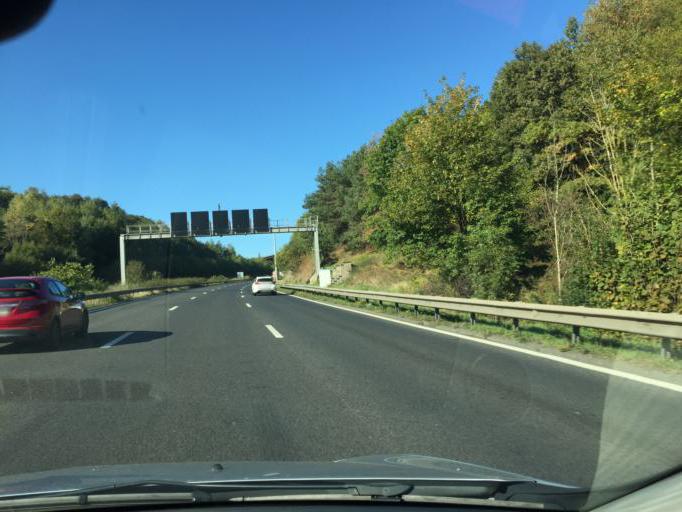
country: LU
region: Luxembourg
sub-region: Canton de Luxembourg
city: Niederanven
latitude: 49.6372
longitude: 6.2466
